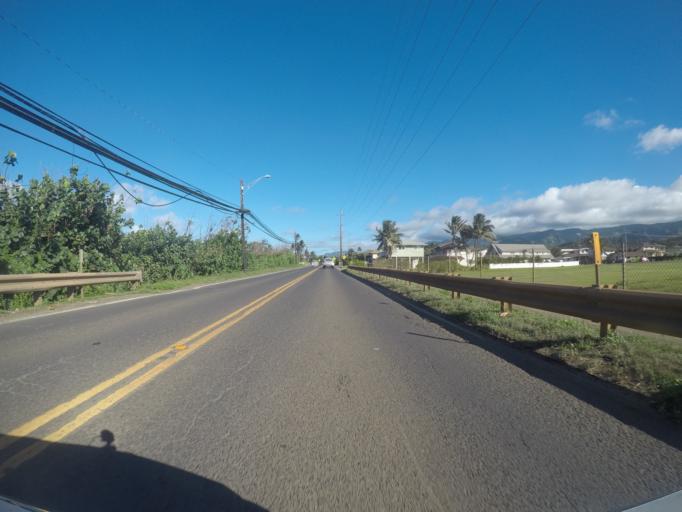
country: US
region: Hawaii
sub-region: Honolulu County
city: La'ie
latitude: 21.6537
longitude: -157.9297
